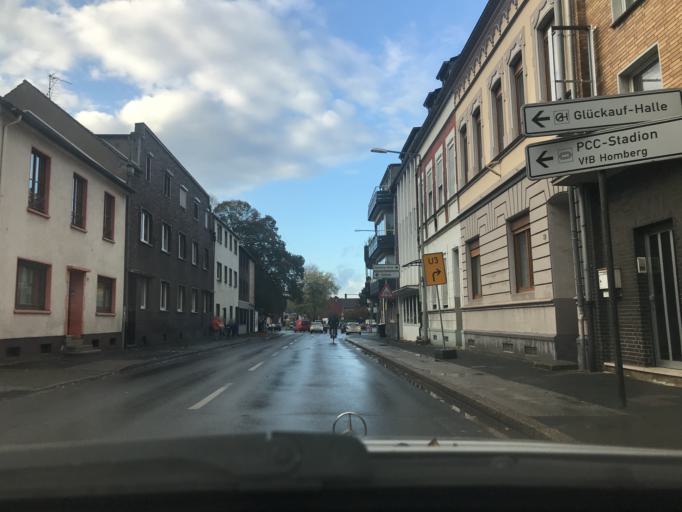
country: DE
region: North Rhine-Westphalia
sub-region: Regierungsbezirk Dusseldorf
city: Hochfeld
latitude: 51.4487
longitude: 6.7041
